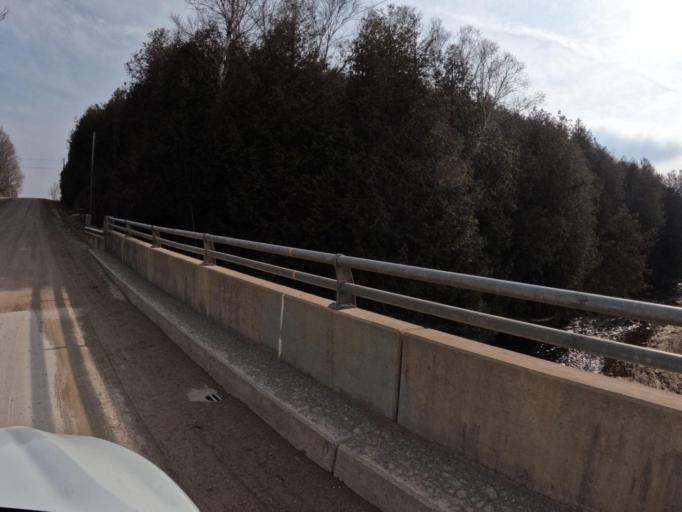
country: CA
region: Ontario
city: Orangeville
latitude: 43.9125
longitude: -80.2706
